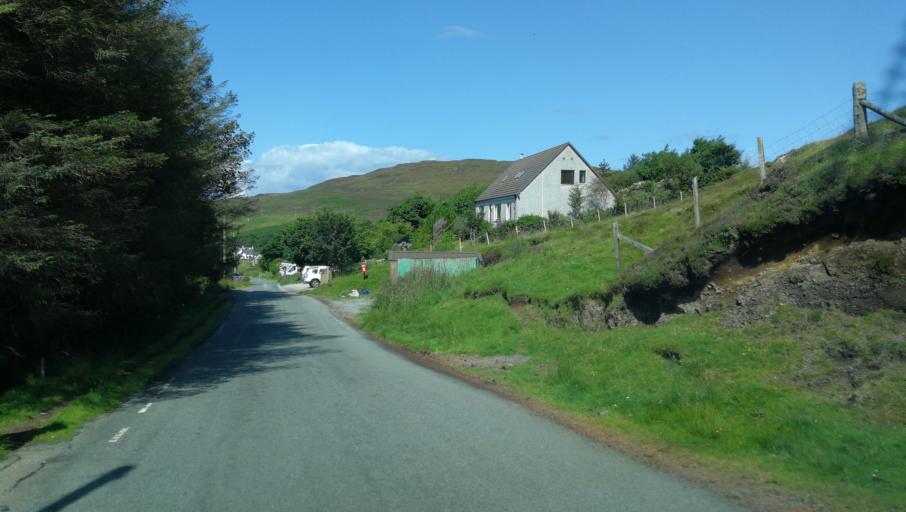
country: GB
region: Scotland
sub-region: Highland
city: Isle of Skye
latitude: 57.4485
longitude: -6.6911
